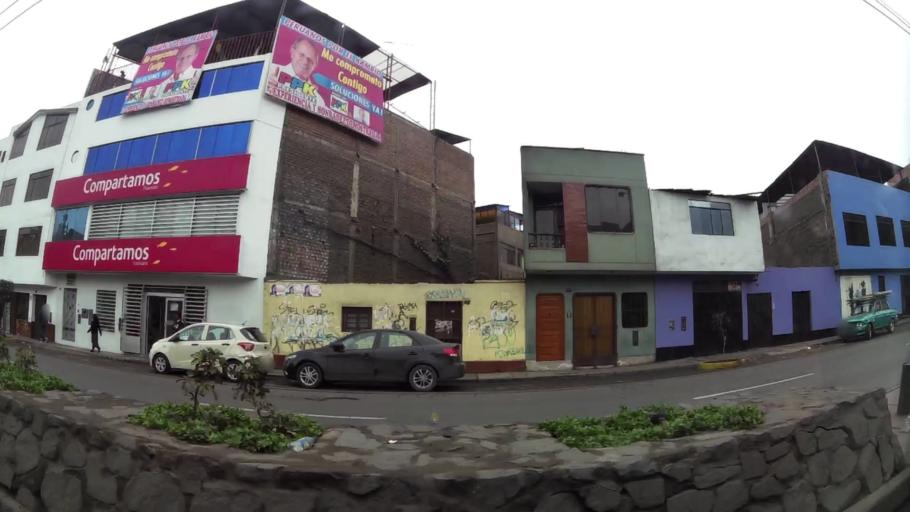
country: PE
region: Lima
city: Lima
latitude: -12.0471
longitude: -77.0000
